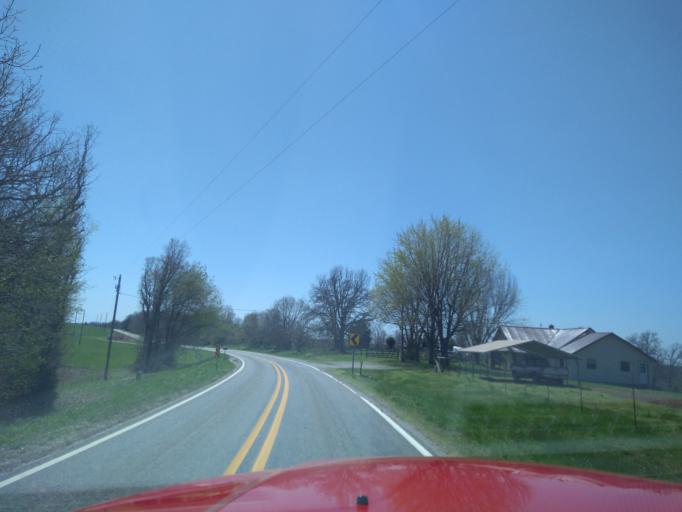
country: US
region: Arkansas
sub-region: Washington County
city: West Fork
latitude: 35.8495
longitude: -94.2774
